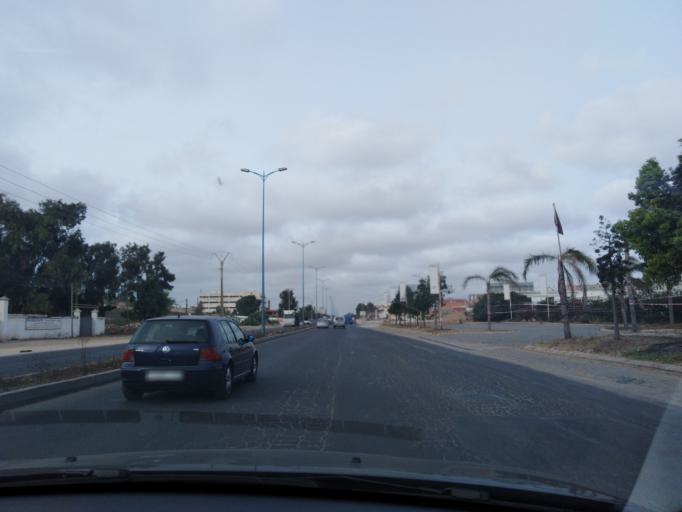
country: MA
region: Grand Casablanca
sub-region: Nouaceur
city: Bouskoura
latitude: 33.5204
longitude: -7.6910
